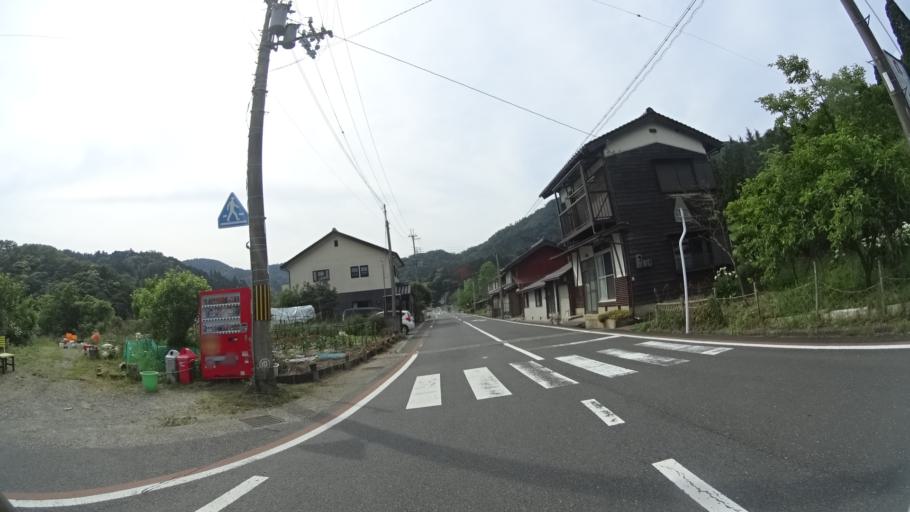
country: JP
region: Kyoto
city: Miyazu
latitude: 35.6723
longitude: 135.2749
